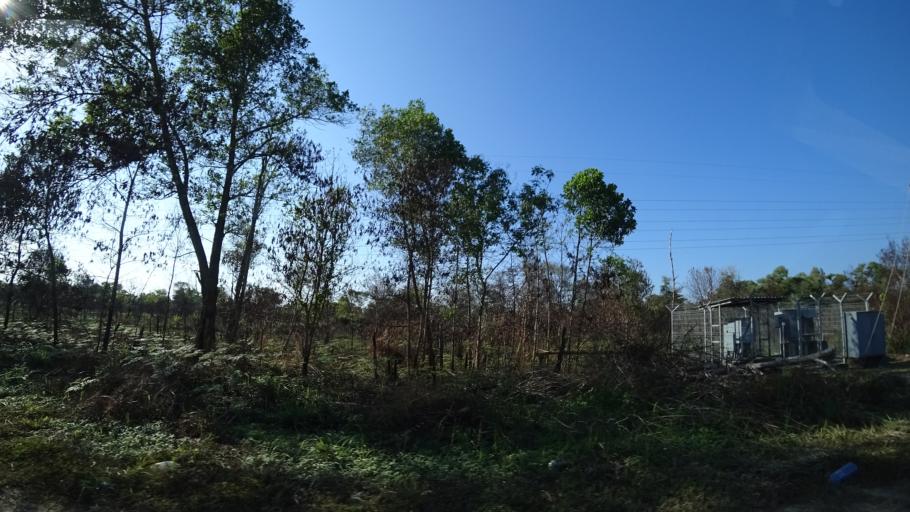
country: BN
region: Tutong
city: Tutong
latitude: 4.7180
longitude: 114.5418
